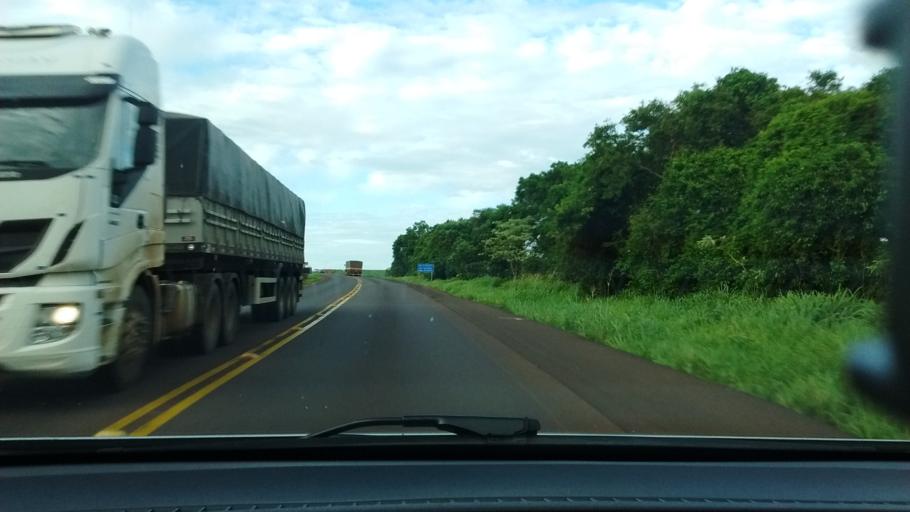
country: BR
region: Parana
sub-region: Cascavel
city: Cascavel
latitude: -25.0653
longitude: -53.5683
